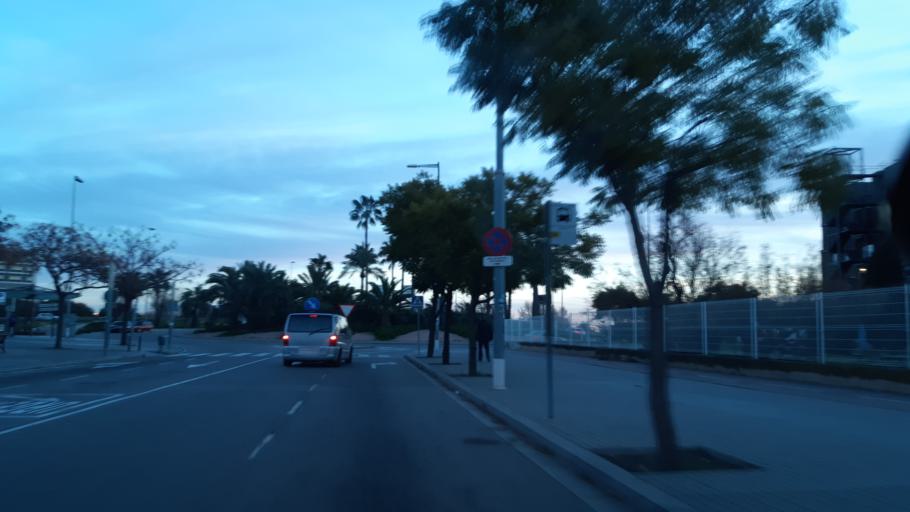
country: ES
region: Catalonia
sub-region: Provincia de Barcelona
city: L'Hospitalet de Llobregat
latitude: 41.3468
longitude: 2.1074
